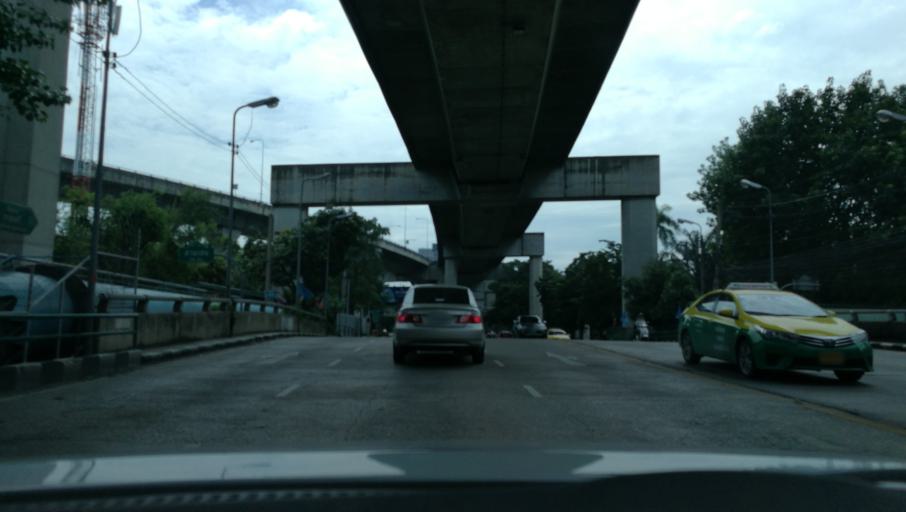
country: TH
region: Bangkok
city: Dusit
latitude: 13.7728
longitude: 100.5302
